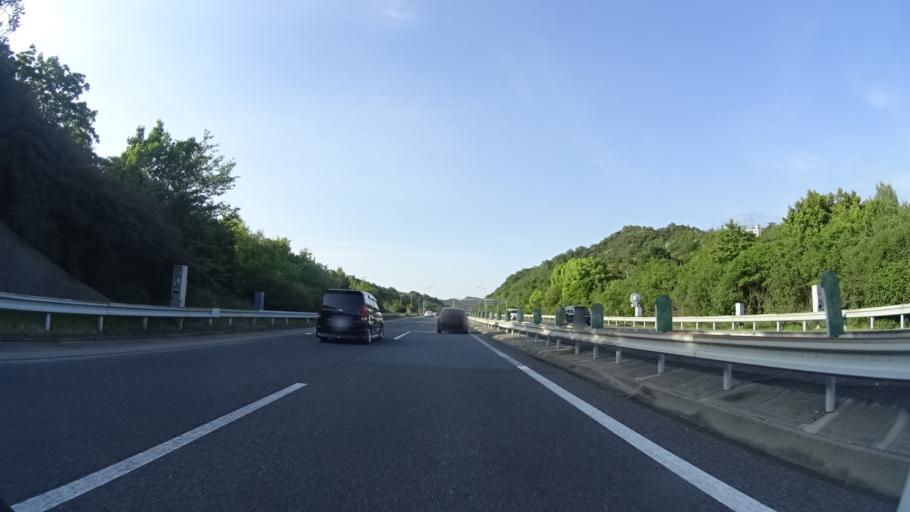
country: JP
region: Ehime
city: Kawanoecho
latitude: 34.0010
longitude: 133.5969
